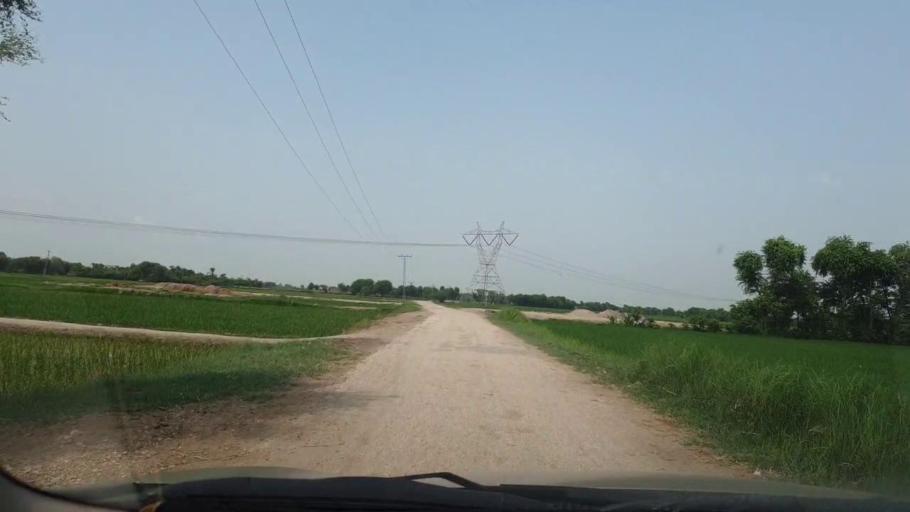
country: PK
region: Sindh
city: Larkana
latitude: 27.5789
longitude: 68.1430
